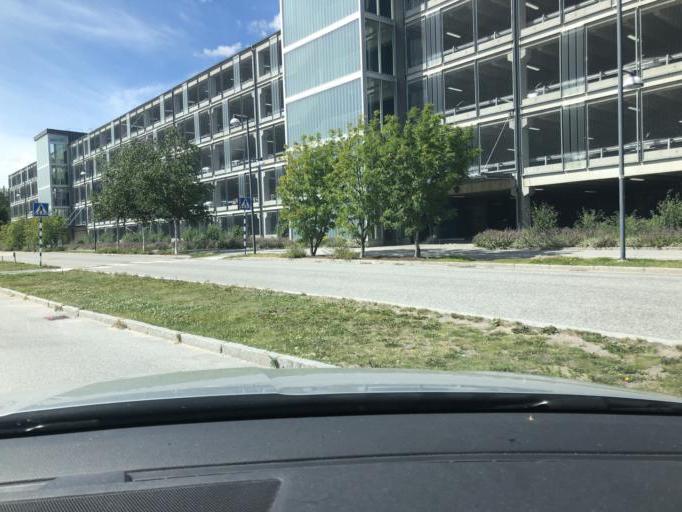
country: SE
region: Stockholm
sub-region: Botkyrka Kommun
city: Tullinge
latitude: 59.2204
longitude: 17.9318
